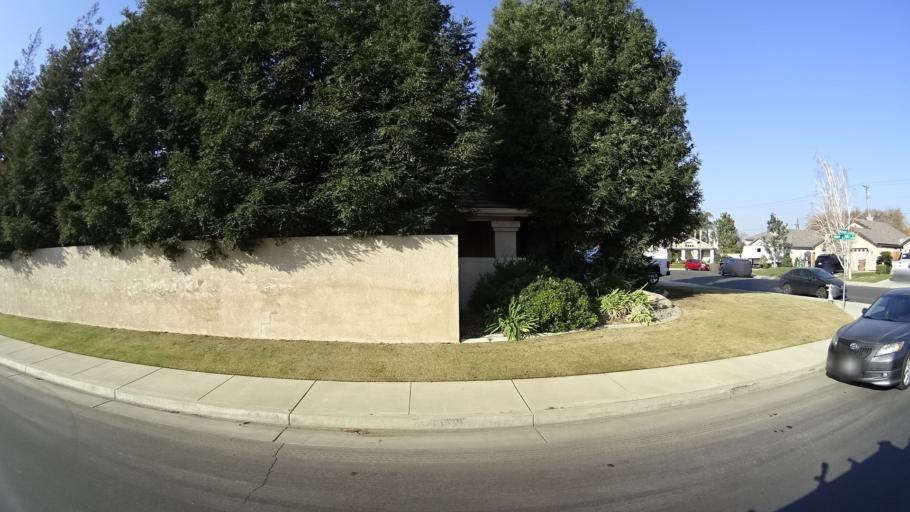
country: US
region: California
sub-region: Kern County
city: Greenacres
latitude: 35.3681
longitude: -119.1141
